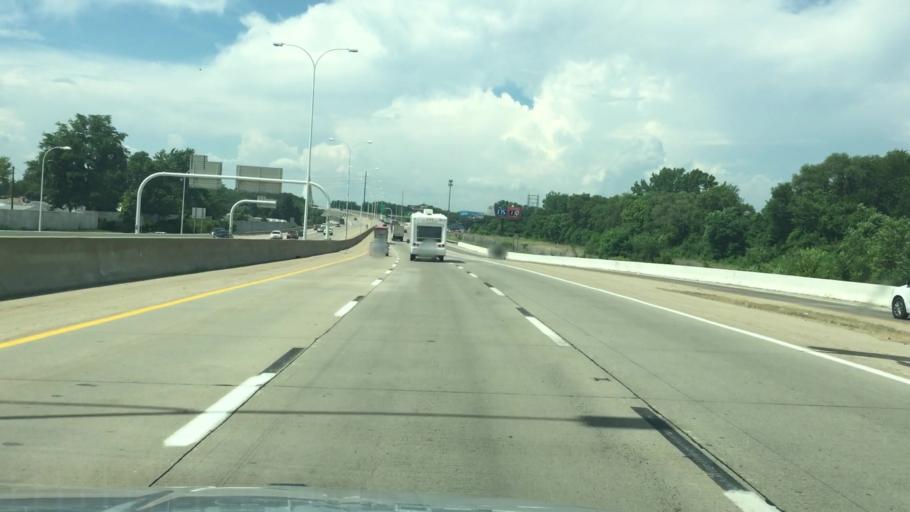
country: US
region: Ohio
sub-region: Lucas County
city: Oregon
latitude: 41.6463
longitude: -83.4990
